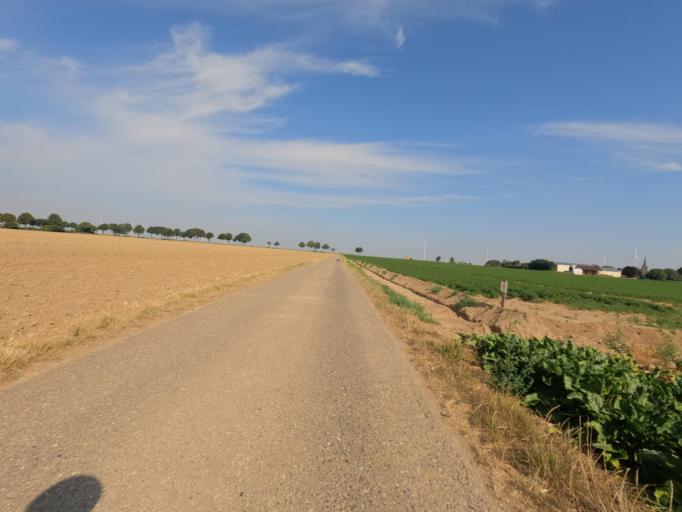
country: DE
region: North Rhine-Westphalia
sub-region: Regierungsbezirk Koln
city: Linnich
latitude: 50.9929
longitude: 6.3416
